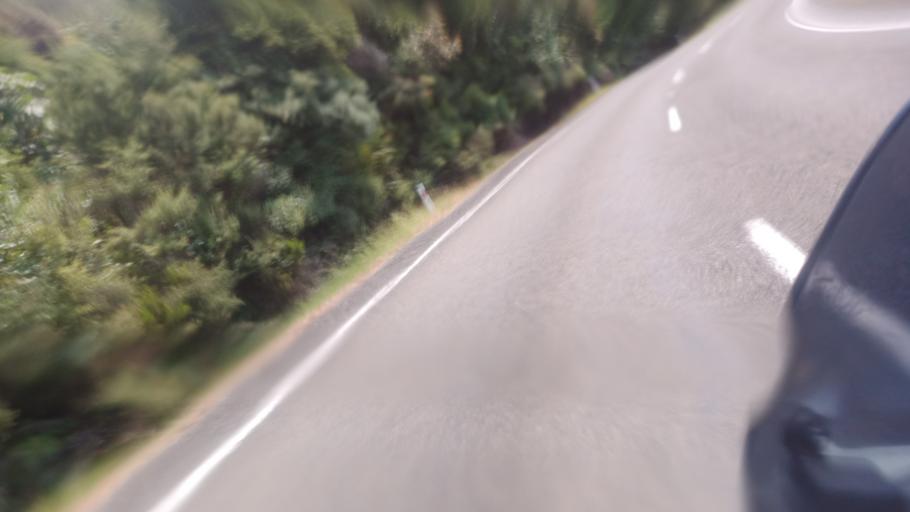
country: NZ
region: Bay of Plenty
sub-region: Opotiki District
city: Opotiki
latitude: -37.5748
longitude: 178.1030
